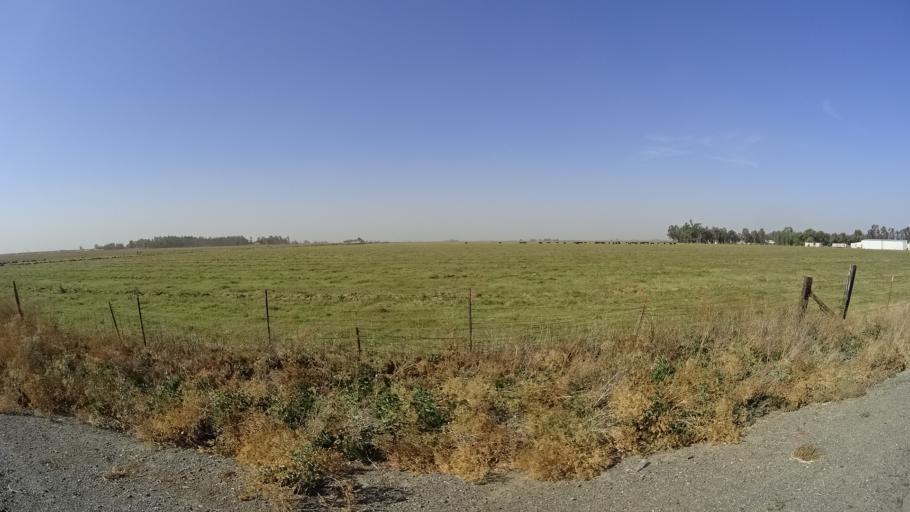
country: US
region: California
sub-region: Yolo County
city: Davis
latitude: 38.4824
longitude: -121.6936
